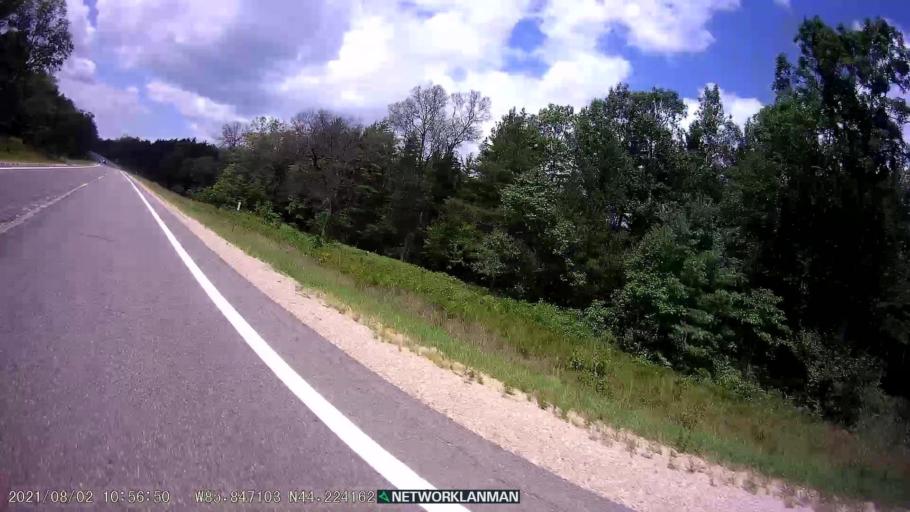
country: US
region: Michigan
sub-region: Lake County
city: Baldwin
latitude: 44.2243
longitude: -85.8473
